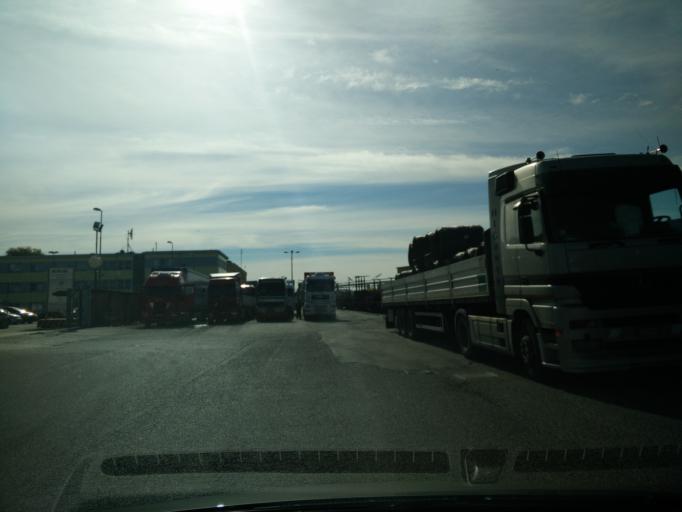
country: IT
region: Veneto
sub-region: Provincia di Venezia
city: Mestre
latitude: 45.4582
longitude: 12.2254
